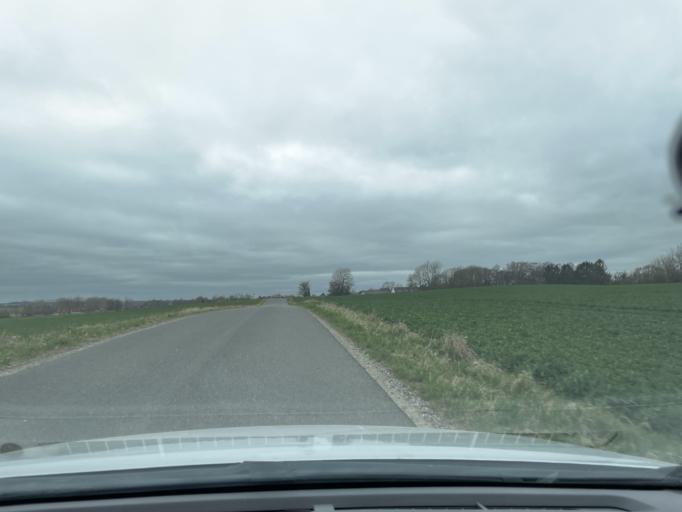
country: DK
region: South Denmark
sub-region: Nyborg Kommune
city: Nyborg
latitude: 55.3540
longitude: 10.7395
